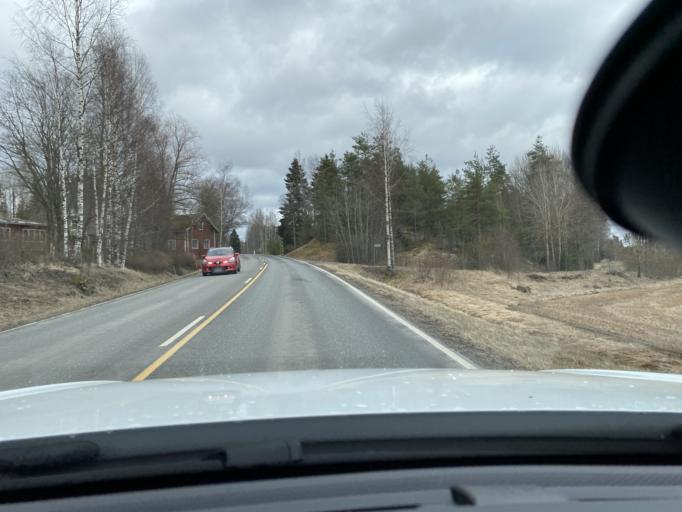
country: FI
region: Pirkanmaa
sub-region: Lounais-Pirkanmaa
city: Punkalaidun
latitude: 61.1030
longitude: 23.1941
